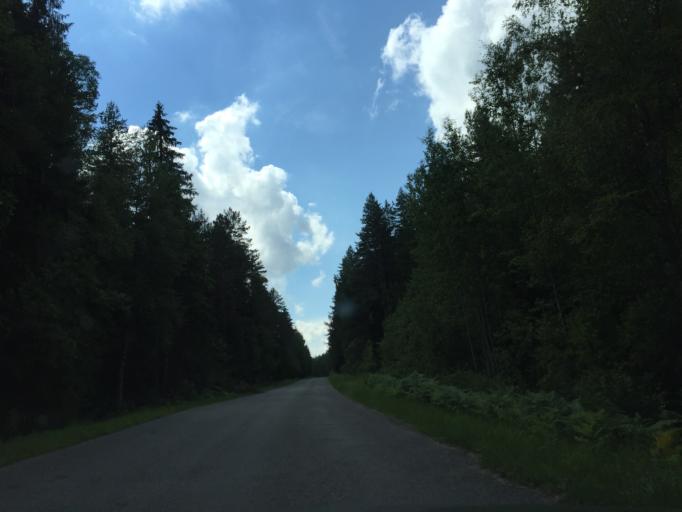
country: LV
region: Ligatne
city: Ligatne
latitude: 57.2495
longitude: 25.0752
